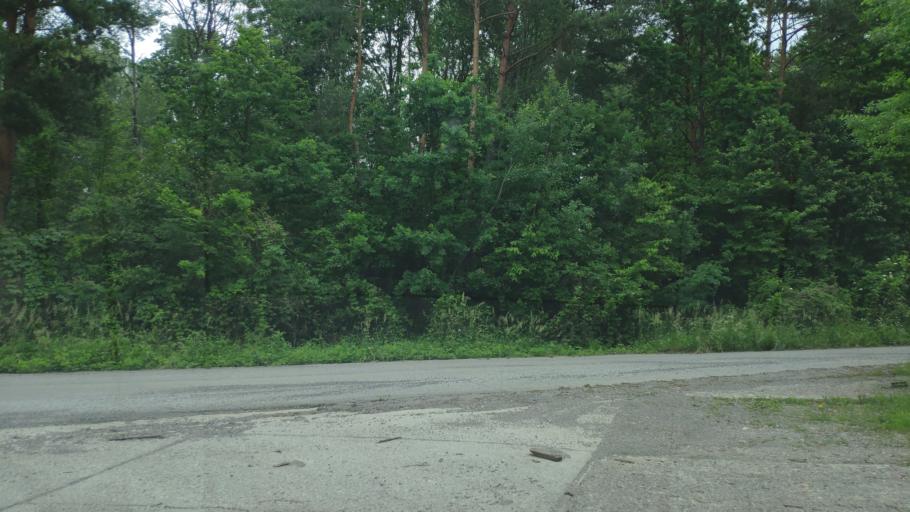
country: SK
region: Presovsky
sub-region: Okres Presov
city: Presov
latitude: 48.9998
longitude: 21.3284
